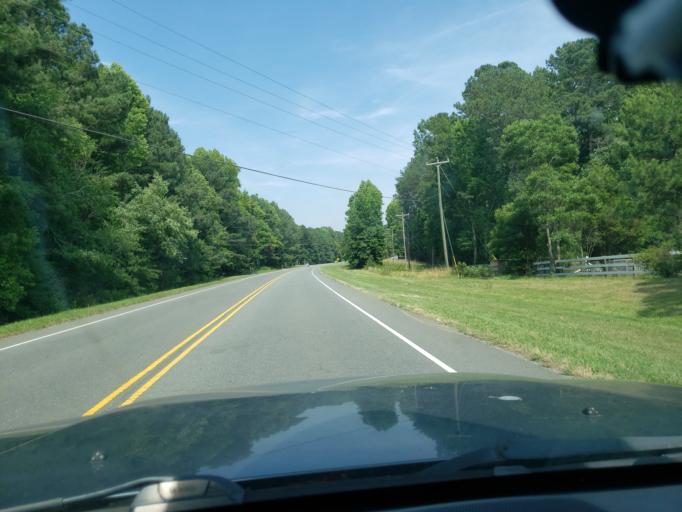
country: US
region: North Carolina
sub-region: Orange County
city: Carrboro
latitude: 35.9270
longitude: -79.1604
